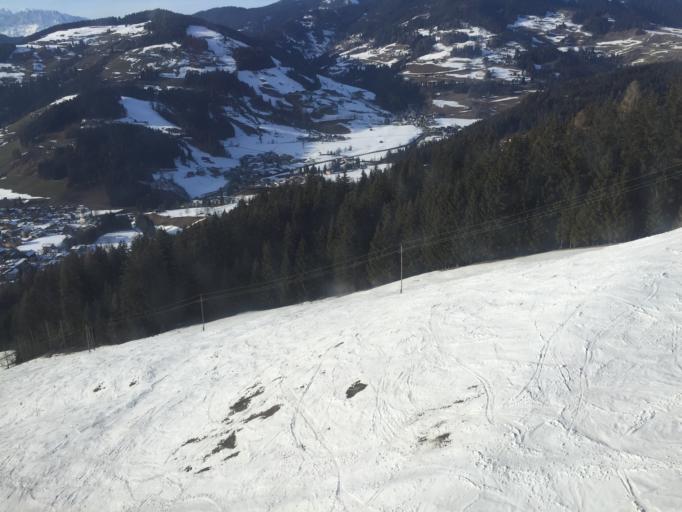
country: AT
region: Salzburg
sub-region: Politischer Bezirk Sankt Johann im Pongau
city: Wagrain
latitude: 47.3291
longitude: 13.3171
